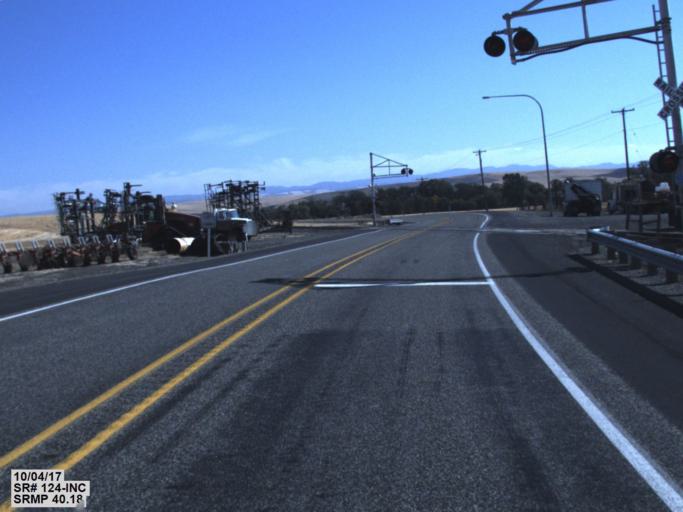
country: US
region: Washington
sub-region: Walla Walla County
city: Waitsburg
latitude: 46.2820
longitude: -118.2363
